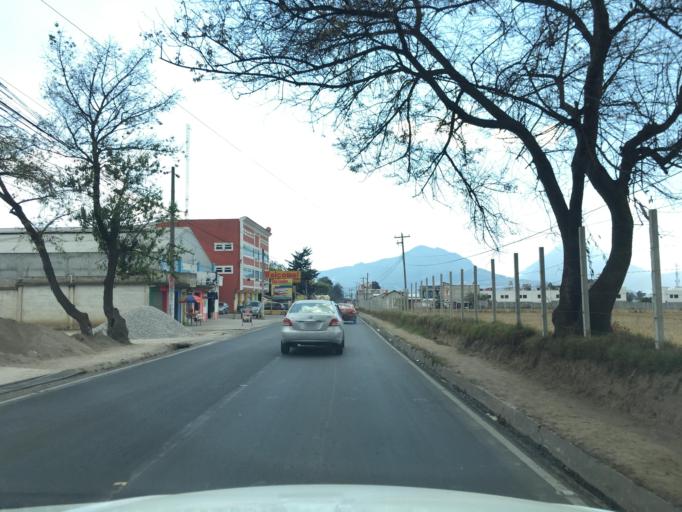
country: GT
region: Quetzaltenango
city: Olintepeque
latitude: 14.8752
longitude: -91.5136
